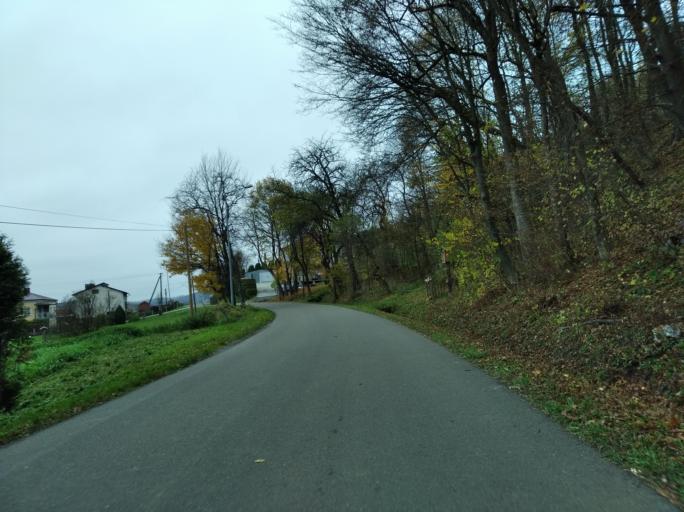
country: PL
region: Subcarpathian Voivodeship
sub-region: Powiat strzyzowski
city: Frysztak
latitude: 49.8324
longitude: 21.6297
